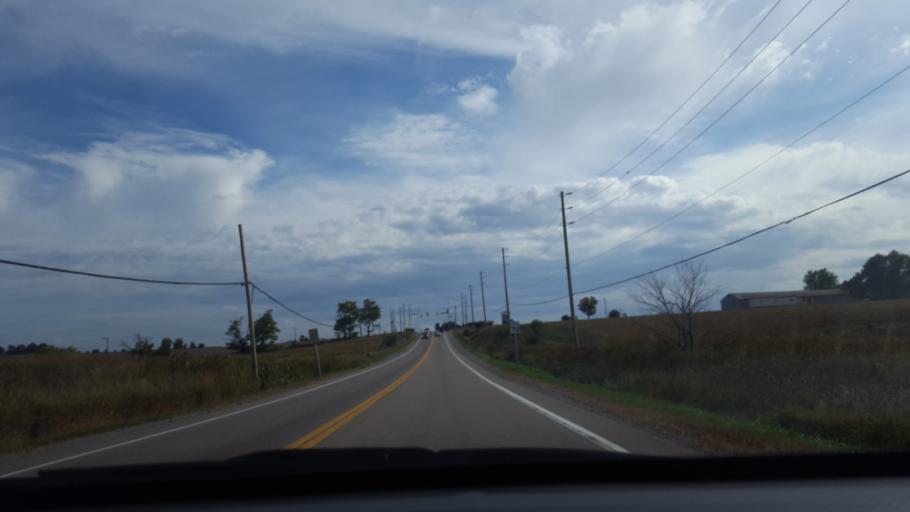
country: CA
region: Ontario
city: Vaughan
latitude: 43.9073
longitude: -79.5503
